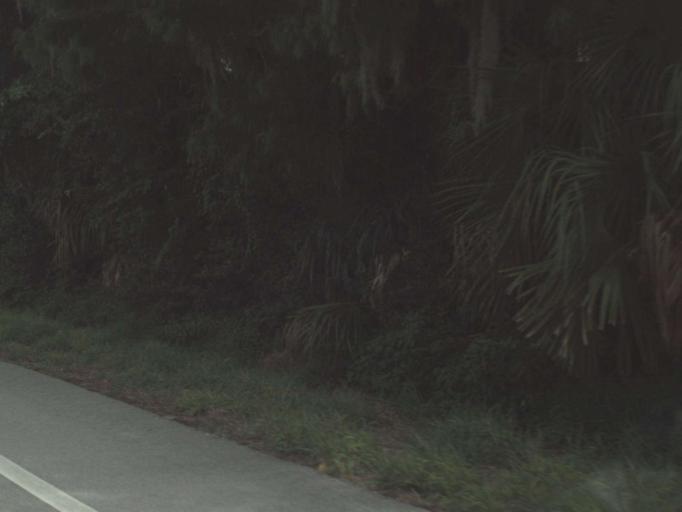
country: US
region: Florida
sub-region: Martin County
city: Indiantown
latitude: 27.0470
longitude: -80.6413
